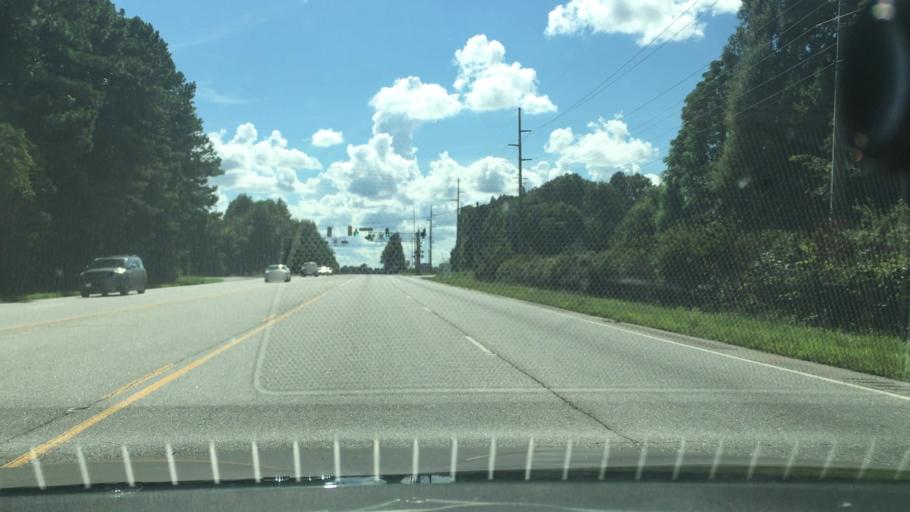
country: US
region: Georgia
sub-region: Spalding County
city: East Griffin
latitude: 33.2336
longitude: -84.2262
